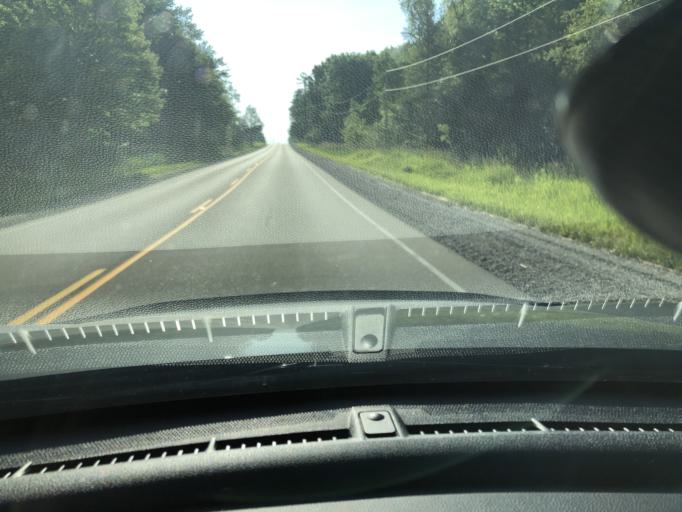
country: CA
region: Ontario
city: Stratford
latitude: 43.4245
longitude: -80.7939
